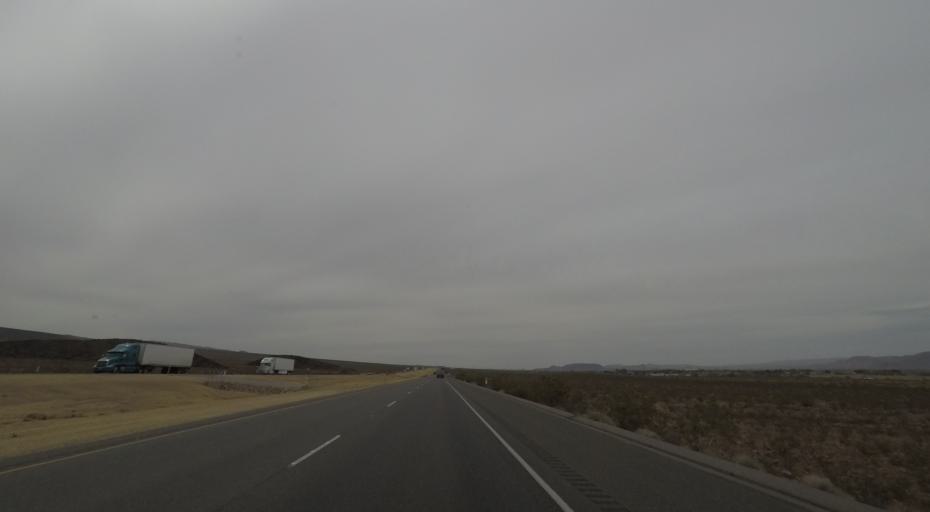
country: US
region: California
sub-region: San Bernardino County
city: Barstow
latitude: 34.8337
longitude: -116.7352
